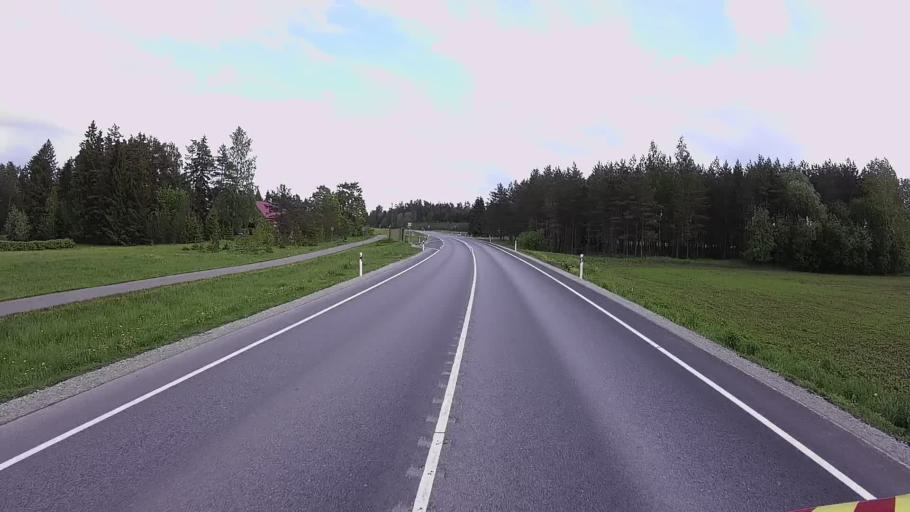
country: EE
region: Laeaene-Virumaa
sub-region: Vinni vald
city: Vinni
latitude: 59.2686
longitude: 26.4403
